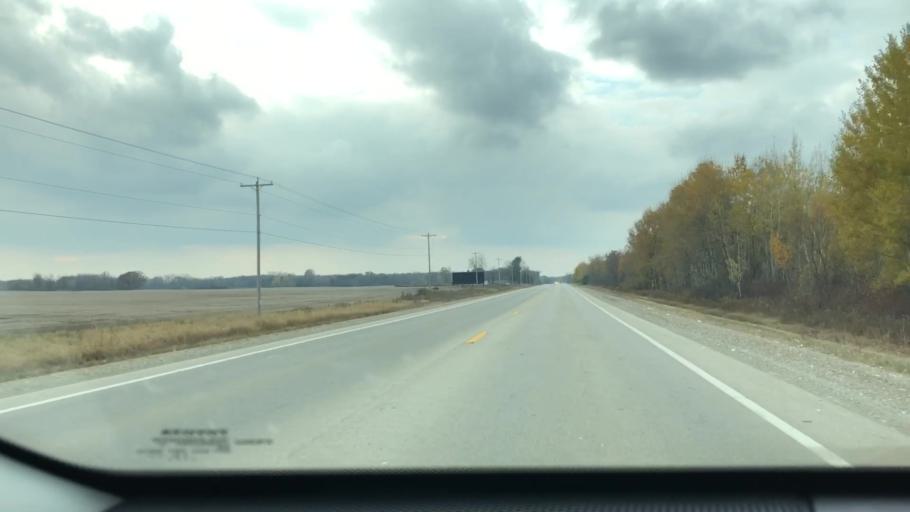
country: US
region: Wisconsin
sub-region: Brown County
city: Oneida
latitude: 44.5021
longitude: -88.2156
